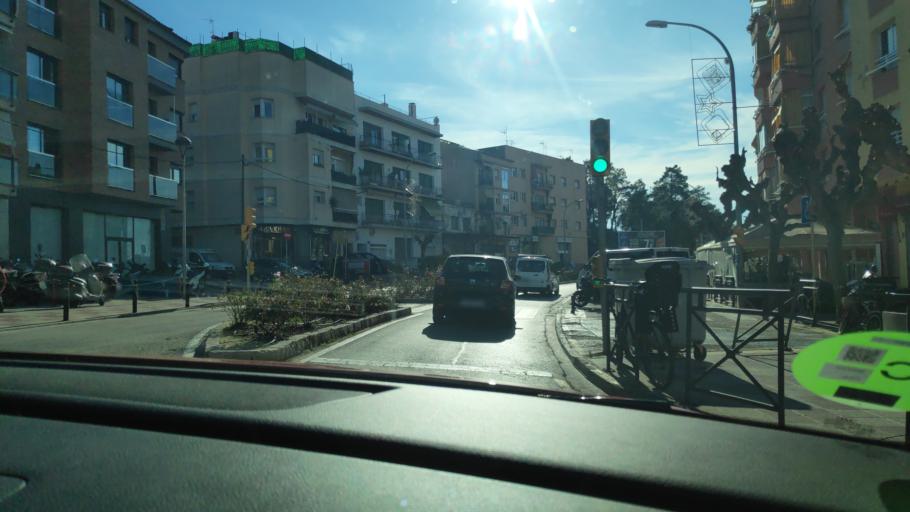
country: ES
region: Catalonia
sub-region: Provincia de Girona
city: Lloret de Mar
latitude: 41.7080
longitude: 2.8417
